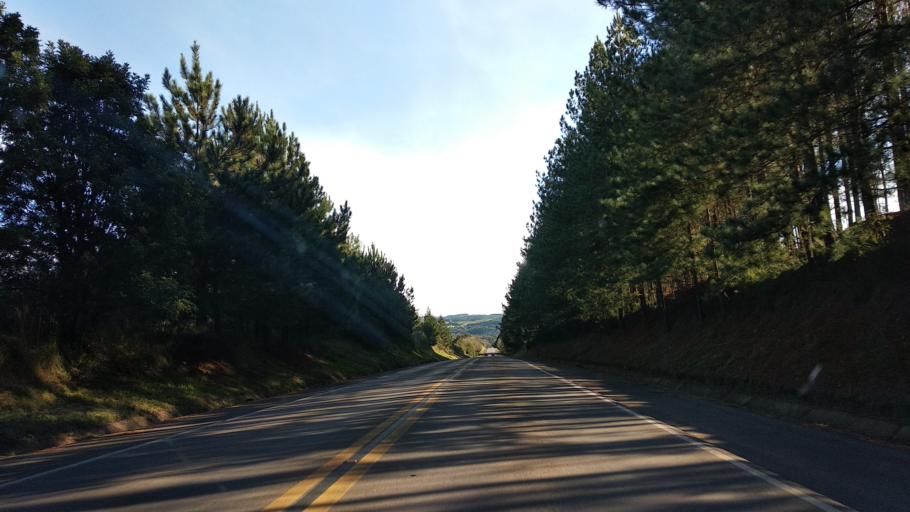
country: BR
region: Santa Catarina
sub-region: Celso Ramos
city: Celso Ramos
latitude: -27.5440
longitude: -51.4236
